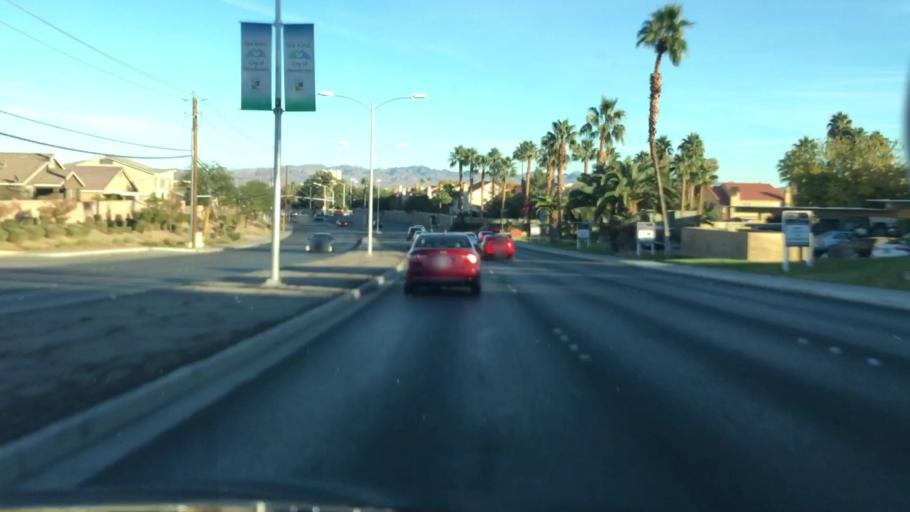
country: US
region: Nevada
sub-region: Clark County
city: Whitney
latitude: 36.0641
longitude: -115.0623
